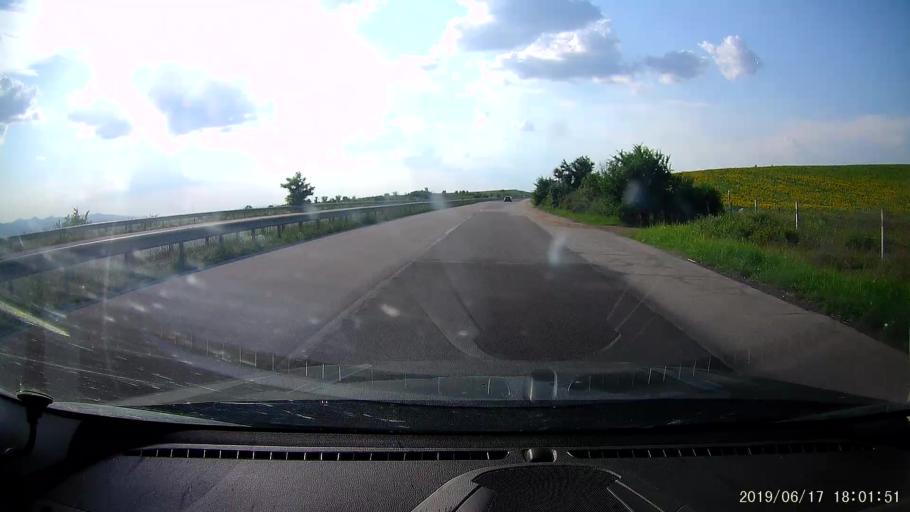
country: BG
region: Khaskovo
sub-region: Obshtina Svilengrad
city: Svilengrad
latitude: 41.7496
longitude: 26.2428
